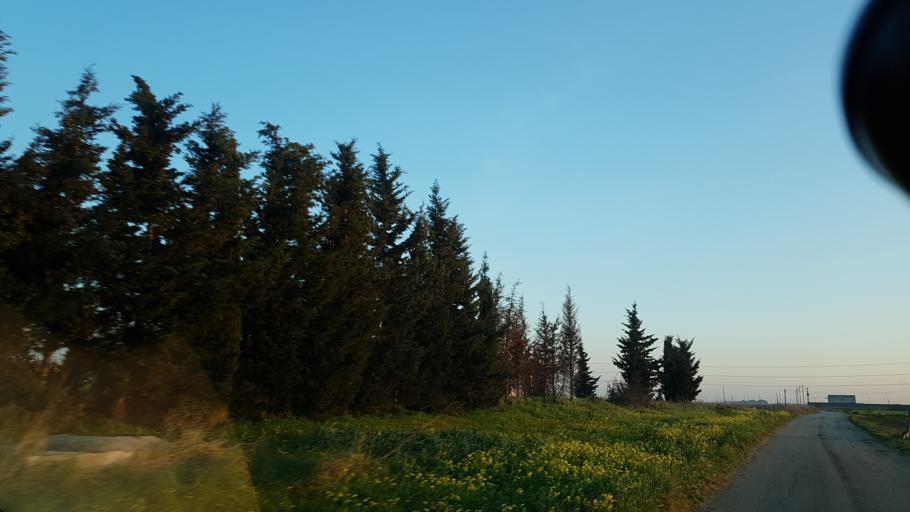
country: IT
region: Apulia
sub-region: Provincia di Brindisi
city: La Rosa
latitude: 40.5989
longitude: 17.9514
